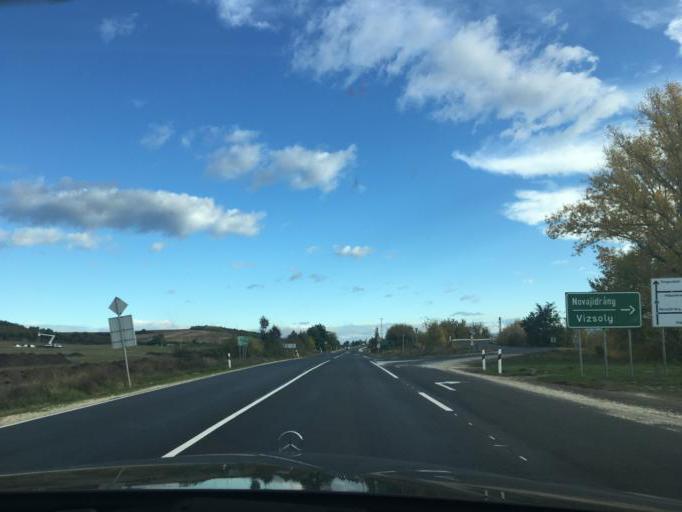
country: HU
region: Borsod-Abauj-Zemplen
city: Encs
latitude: 48.3884
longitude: 21.1559
